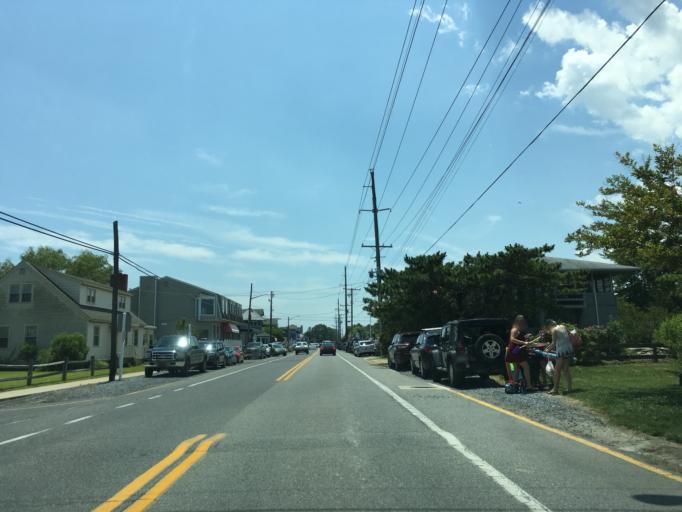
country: US
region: Delaware
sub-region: Sussex County
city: Bethany Beach
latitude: 38.5412
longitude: -75.0575
